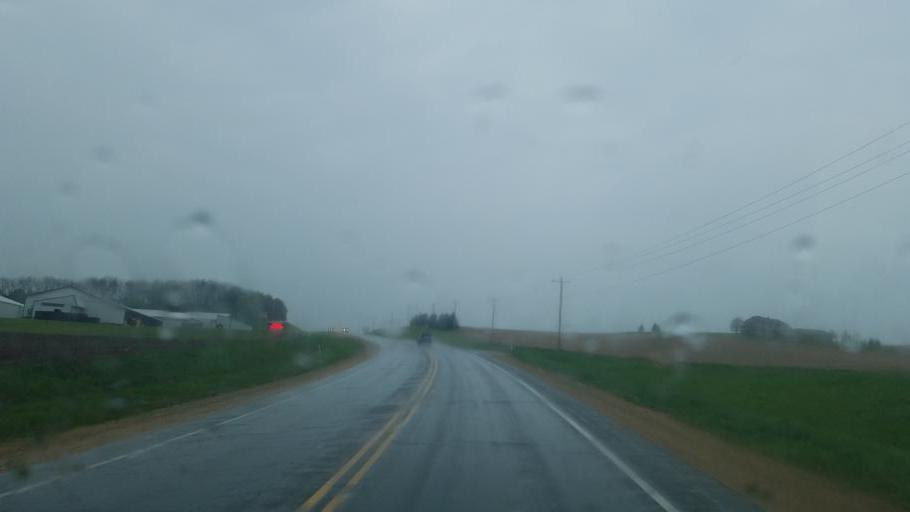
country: US
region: Wisconsin
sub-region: Sauk County
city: Reedsburg
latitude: 43.5659
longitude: -90.0866
